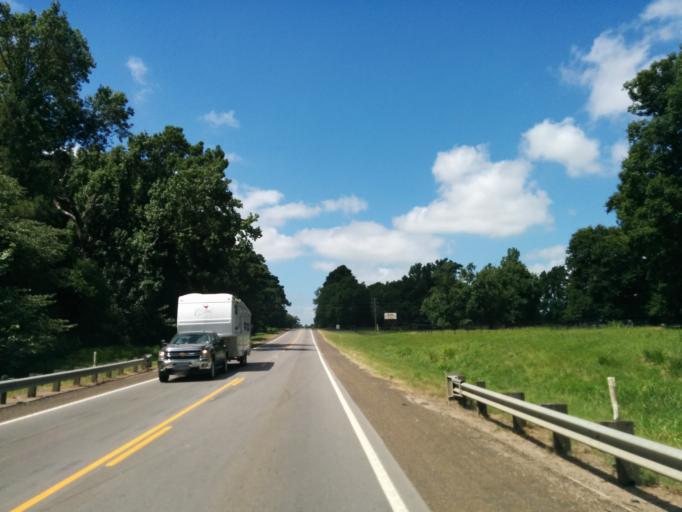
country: US
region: Texas
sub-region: Houston County
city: Crockett
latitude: 31.3064
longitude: -95.4862
